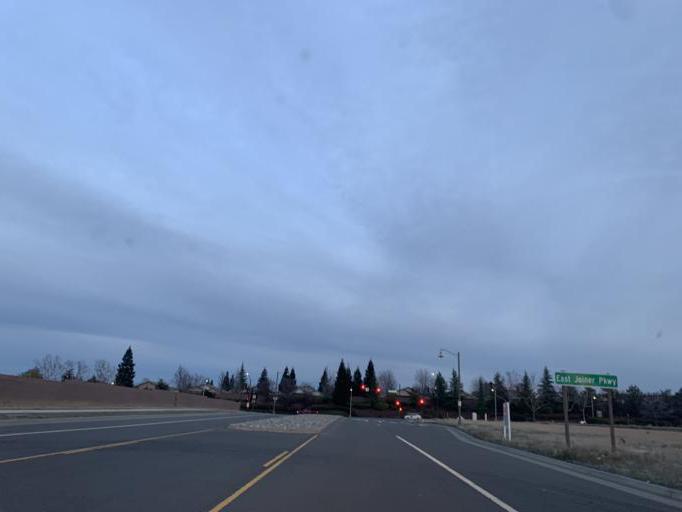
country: US
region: California
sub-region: Placer County
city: Lincoln
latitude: 38.8598
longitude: -121.2862
